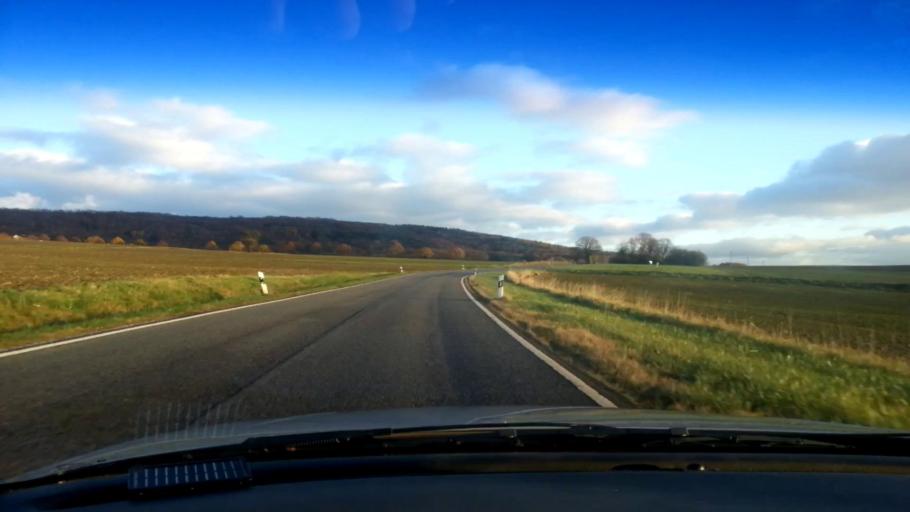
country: DE
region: Bavaria
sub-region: Upper Franconia
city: Buttenheim
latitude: 49.8417
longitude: 11.0255
